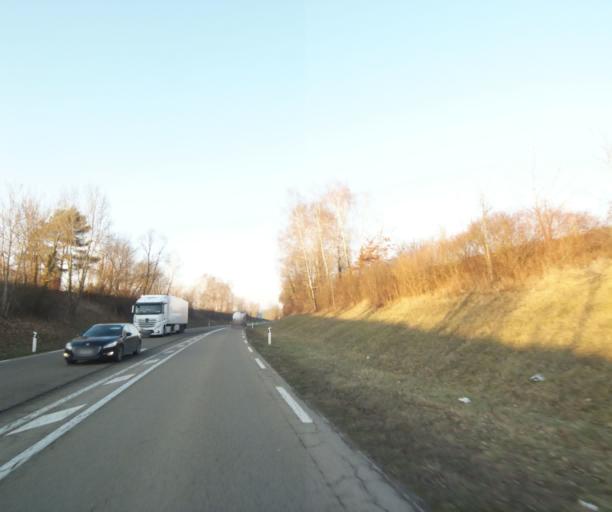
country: FR
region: Champagne-Ardenne
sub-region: Departement de la Haute-Marne
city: Bienville
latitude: 48.5828
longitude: 5.0285
